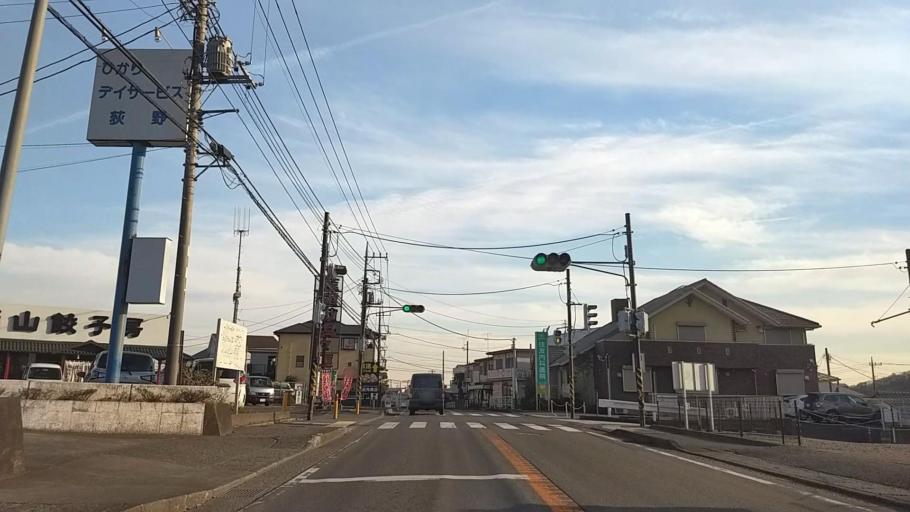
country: JP
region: Kanagawa
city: Atsugi
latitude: 35.4950
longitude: 139.3169
